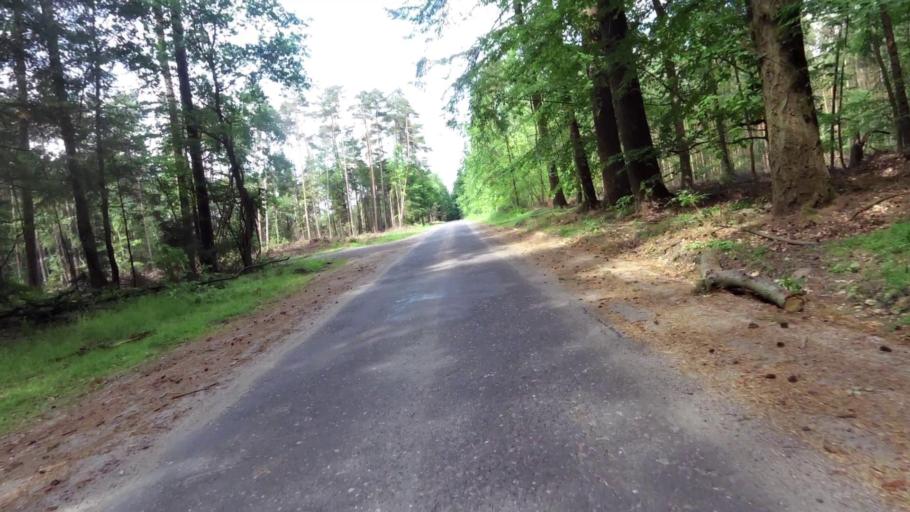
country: PL
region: West Pomeranian Voivodeship
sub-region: Powiat mysliborski
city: Debno
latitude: 52.8028
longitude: 14.6588
